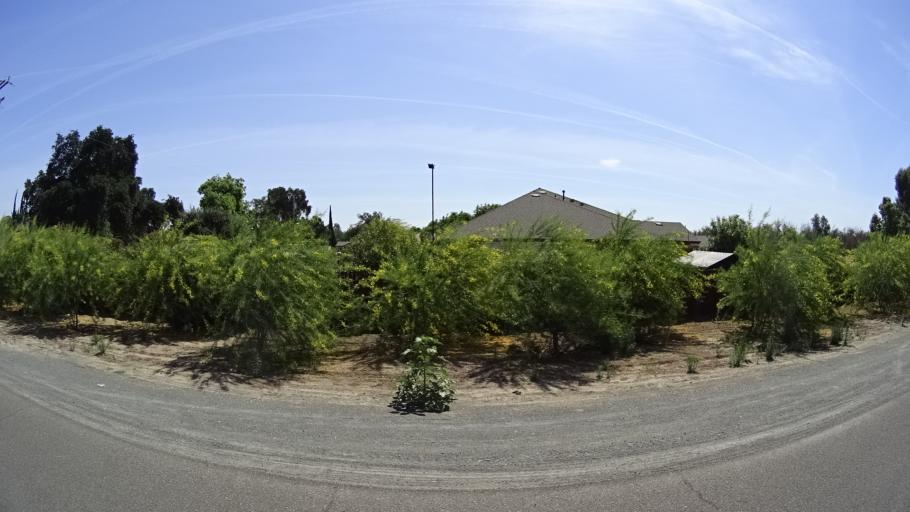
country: US
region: California
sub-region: Kings County
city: Armona
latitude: 36.3416
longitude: -119.7090
